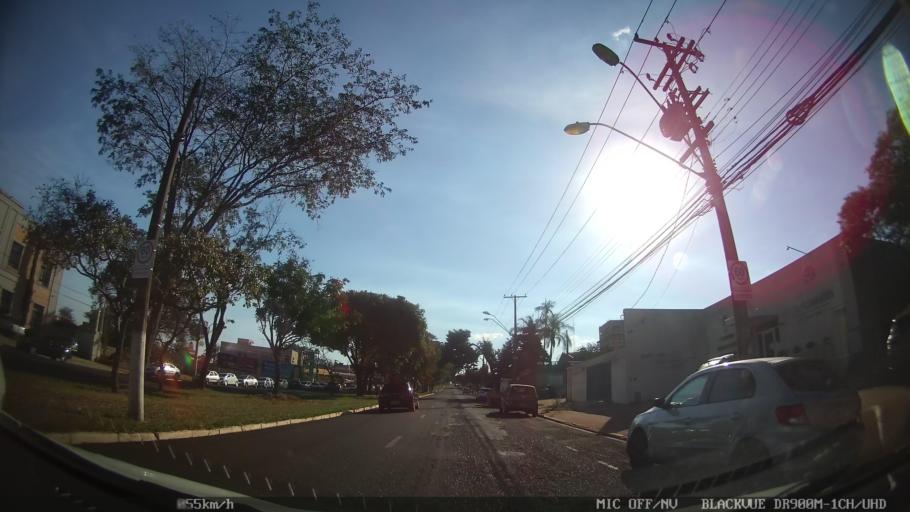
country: BR
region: Sao Paulo
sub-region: Ribeirao Preto
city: Ribeirao Preto
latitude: -21.2048
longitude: -47.7733
